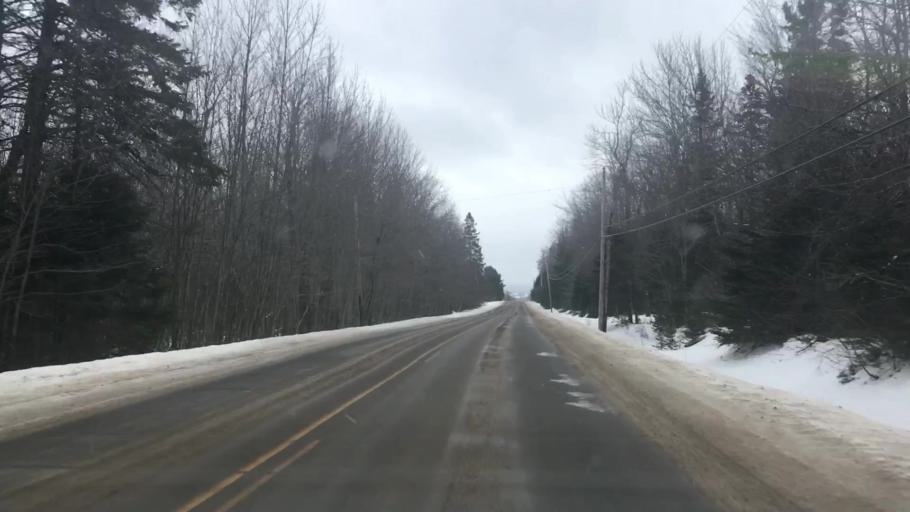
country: US
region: Maine
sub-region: Washington County
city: East Machias
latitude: 44.9841
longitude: -67.4562
